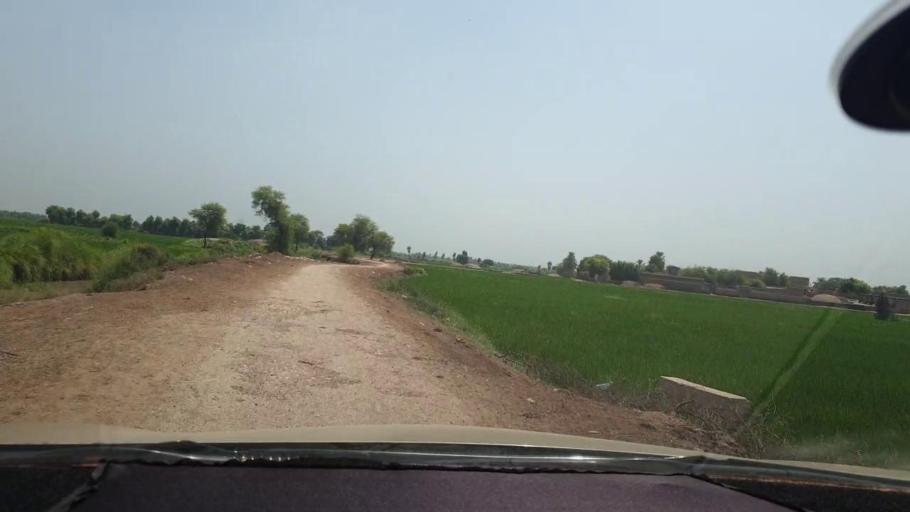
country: PK
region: Sindh
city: Kambar
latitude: 27.6760
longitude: 67.9428
